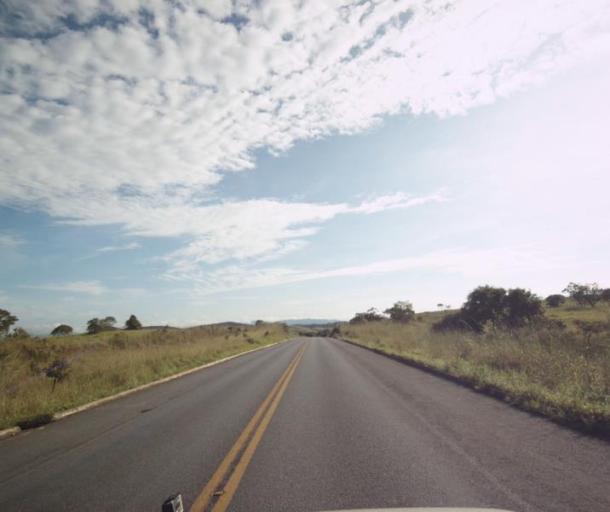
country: BR
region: Goias
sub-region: Pirenopolis
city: Pirenopolis
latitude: -15.6367
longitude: -48.6731
